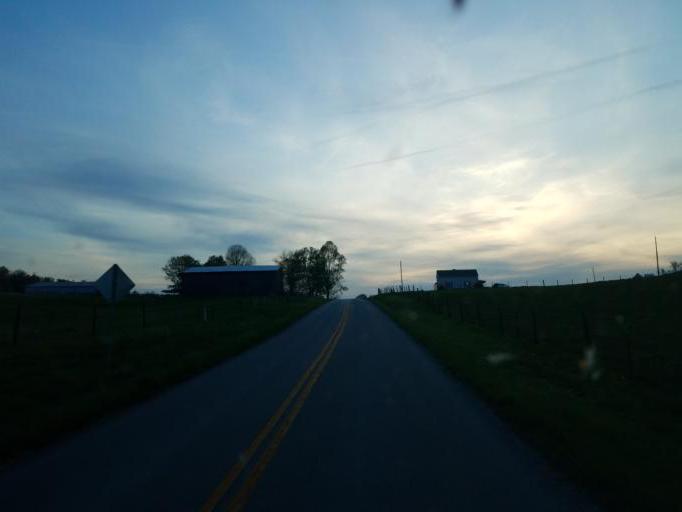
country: US
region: Kentucky
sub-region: Hart County
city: Munfordville
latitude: 37.2502
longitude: -85.7659
